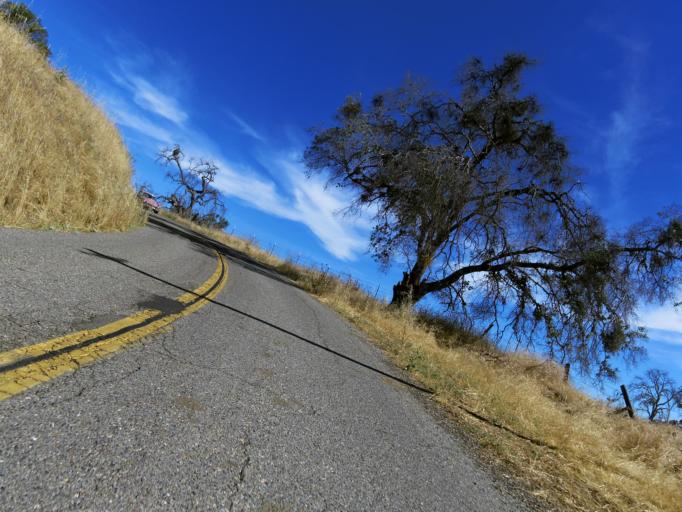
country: US
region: California
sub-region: Mariposa County
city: Mariposa
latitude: 37.3646
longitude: -119.9648
